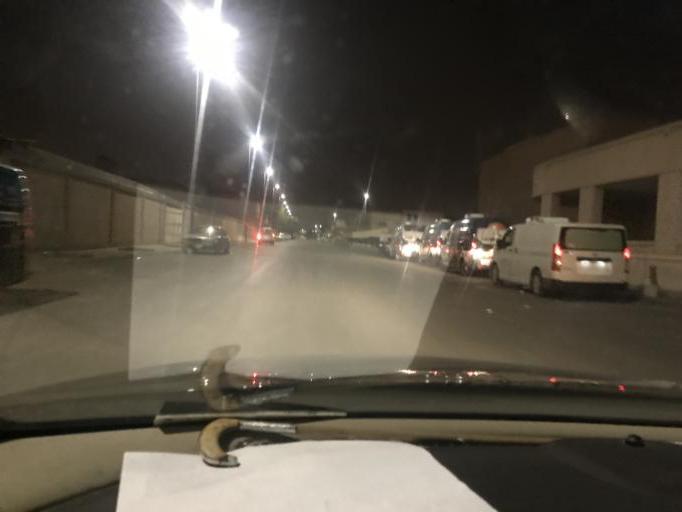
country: SA
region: Ar Riyad
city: Riyadh
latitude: 24.7235
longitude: 46.7741
